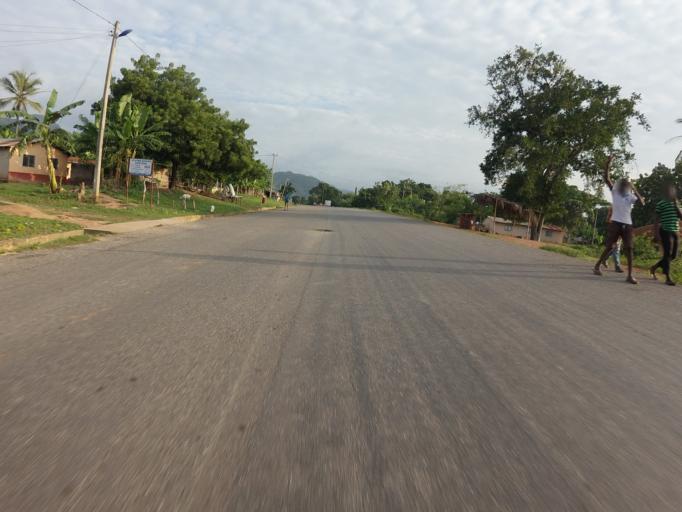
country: GH
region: Volta
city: Kpandu
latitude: 6.8854
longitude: 0.4218
